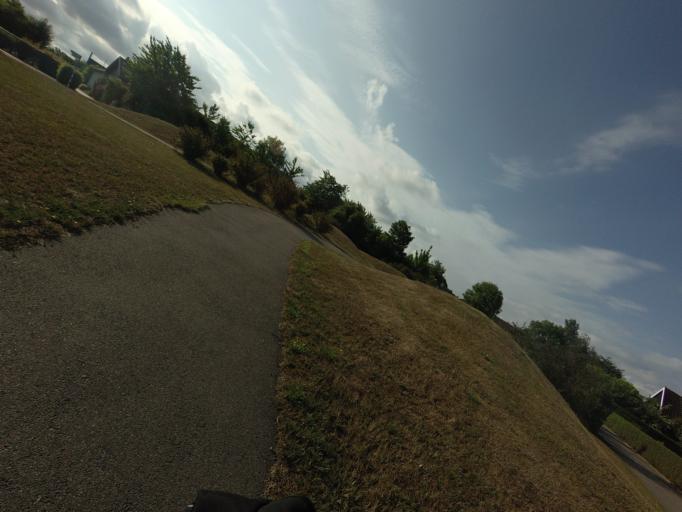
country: SE
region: Skane
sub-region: Hoganas Kommun
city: Hoganas
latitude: 56.1608
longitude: 12.5742
